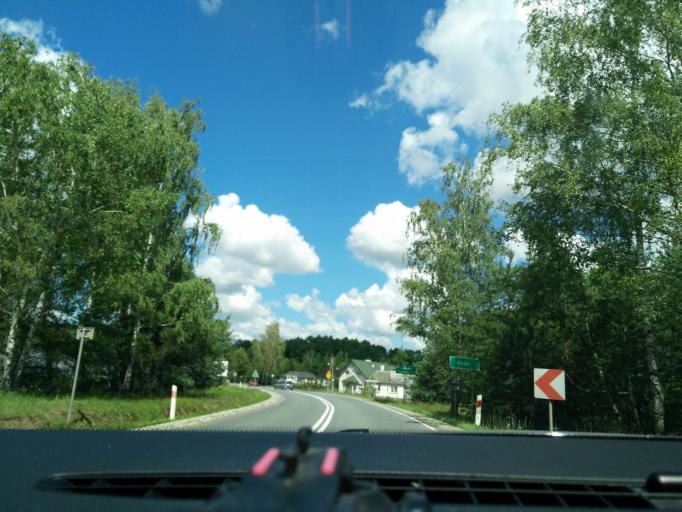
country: PL
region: Masovian Voivodeship
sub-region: Powiat losicki
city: Sarnaki
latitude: 52.3571
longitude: 22.8731
